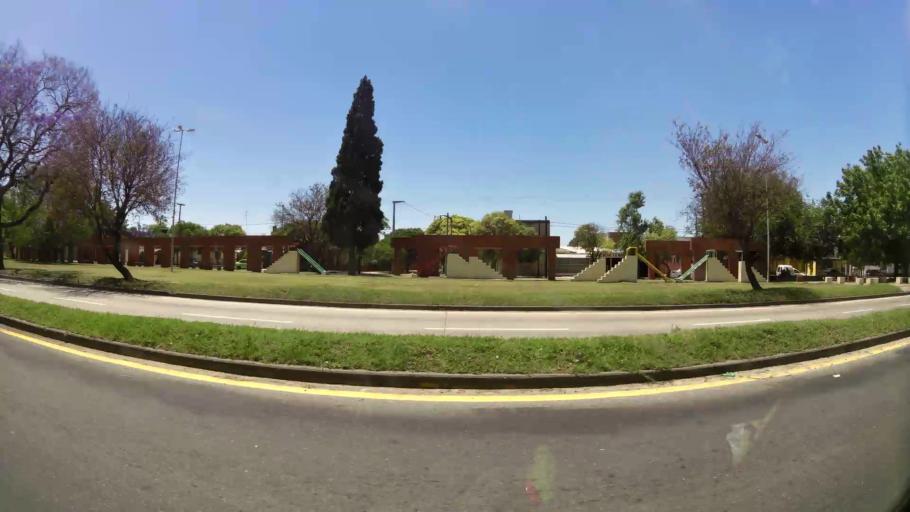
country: AR
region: Cordoba
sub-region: Departamento de Capital
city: Cordoba
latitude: -31.4407
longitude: -64.1274
